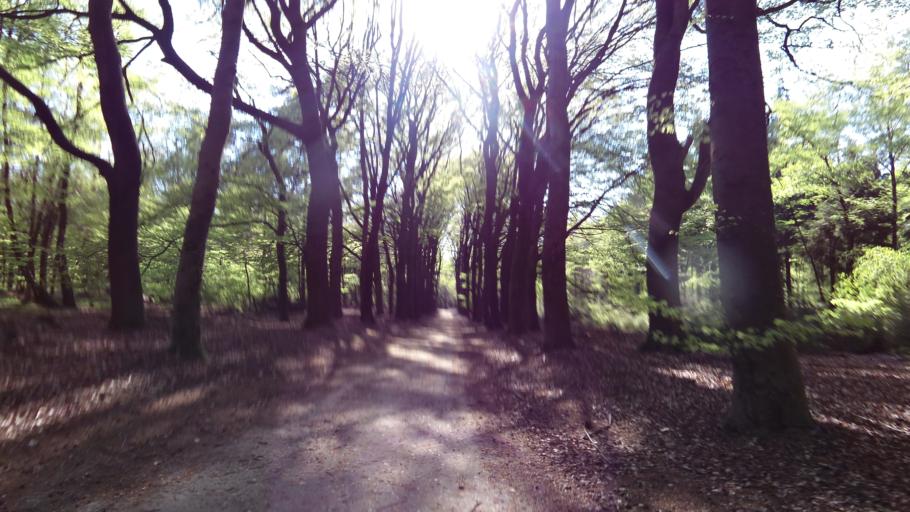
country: NL
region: Gelderland
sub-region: Gemeente Rozendaal
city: Rozendaal
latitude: 52.0177
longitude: 5.9499
